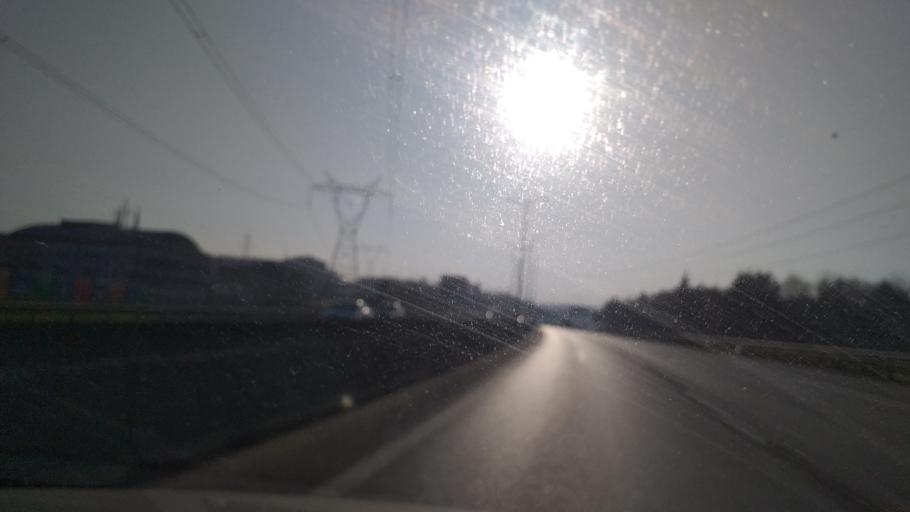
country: TR
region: Istanbul
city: Samandira
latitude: 40.9775
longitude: 29.2093
